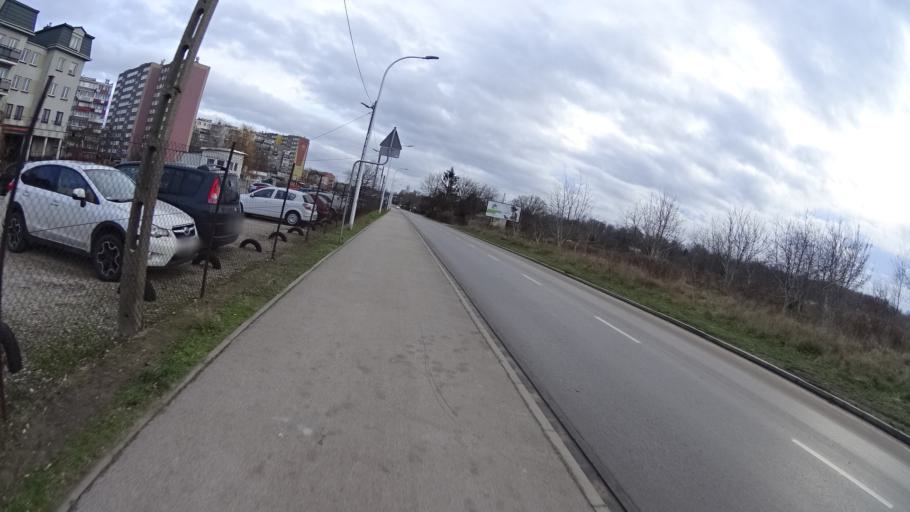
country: PL
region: Masovian Voivodeship
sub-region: Powiat pruszkowski
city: Granica
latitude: 52.1561
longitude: 20.7859
